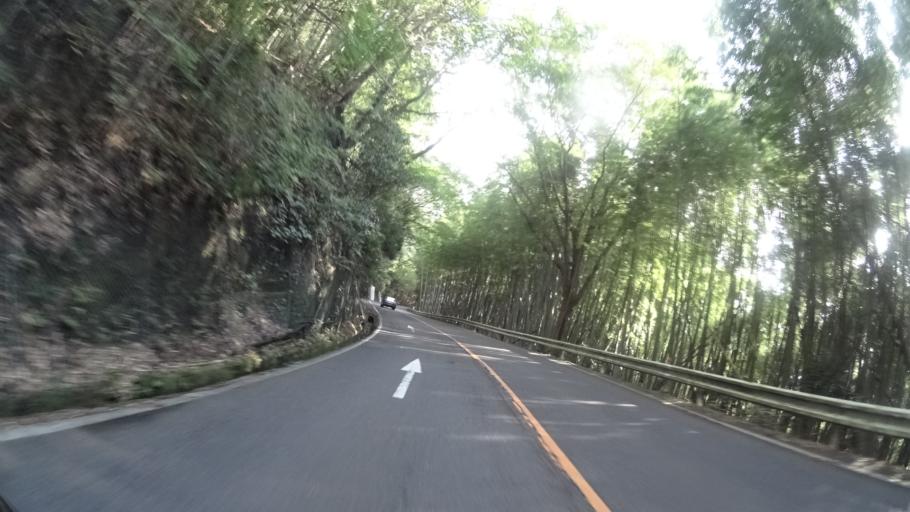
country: JP
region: Oita
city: Beppu
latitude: 33.2681
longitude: 131.3697
